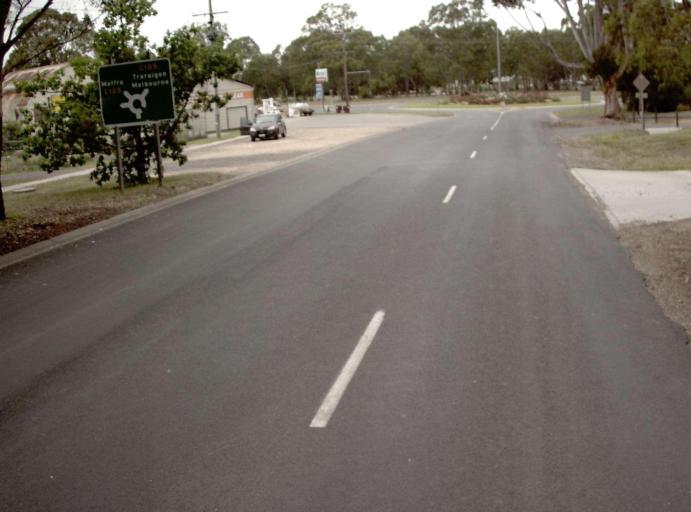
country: AU
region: Victoria
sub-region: Wellington
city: Heyfield
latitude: -37.9774
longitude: 146.7836
